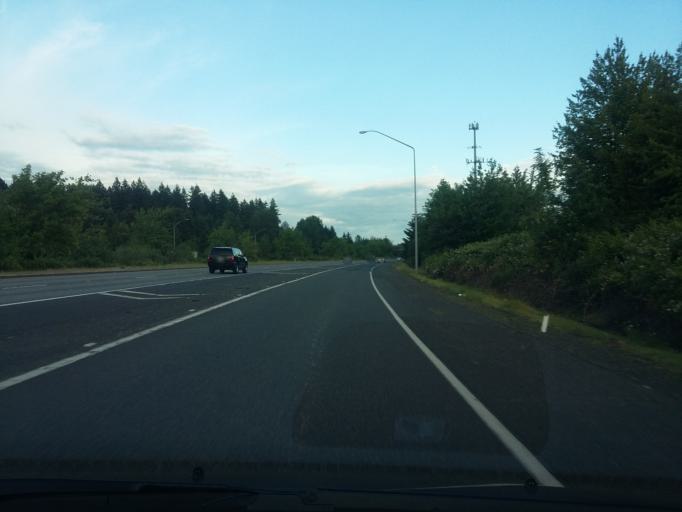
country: US
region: Washington
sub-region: Clark County
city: Barberton
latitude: 45.6814
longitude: -122.5910
